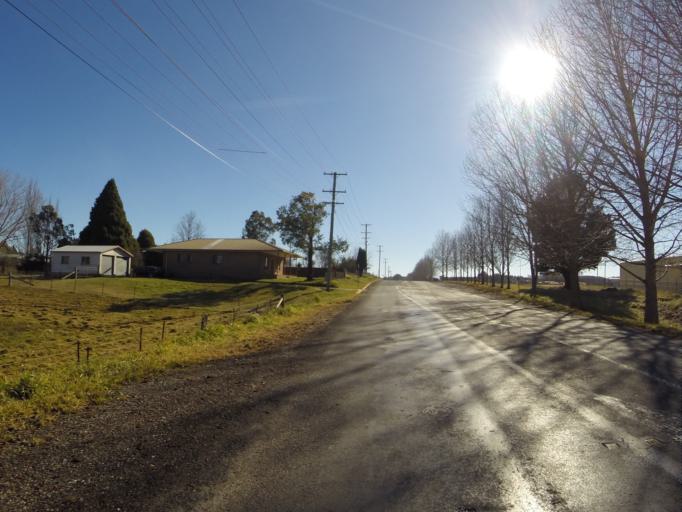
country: AU
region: New South Wales
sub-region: Oberon
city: Oberon
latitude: -33.6918
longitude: 149.8566
